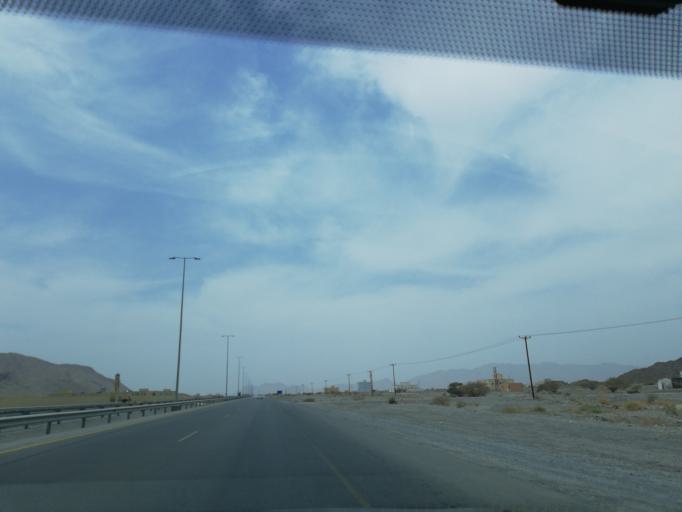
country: OM
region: Muhafazat ad Dakhiliyah
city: Izki
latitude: 22.8915
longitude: 57.6722
